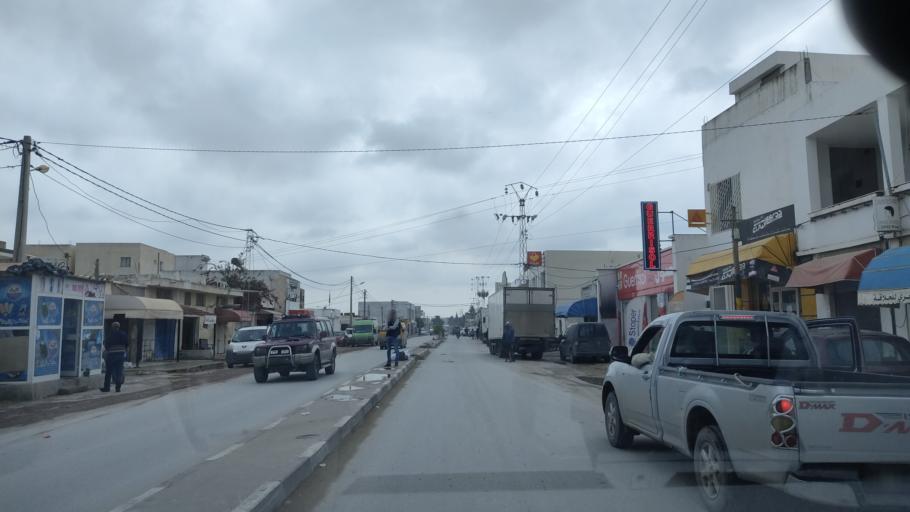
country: TN
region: Ariana
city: Ariana
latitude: 36.8874
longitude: 10.2166
